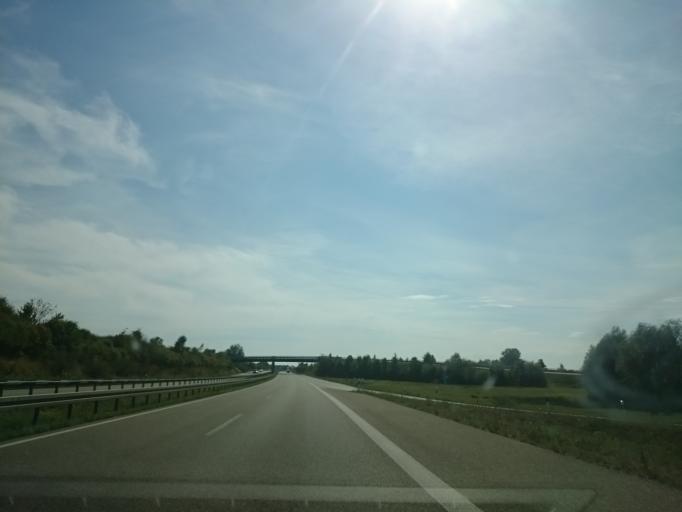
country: DE
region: Bavaria
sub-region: Swabia
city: Biberbach
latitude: 48.5237
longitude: 10.8339
